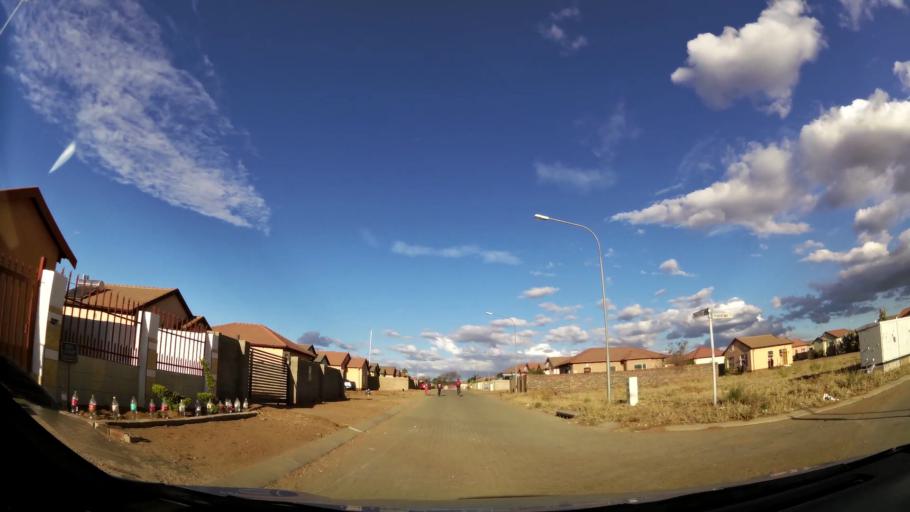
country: ZA
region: Limpopo
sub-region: Capricorn District Municipality
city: Polokwane
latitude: -23.9203
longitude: 29.4197
